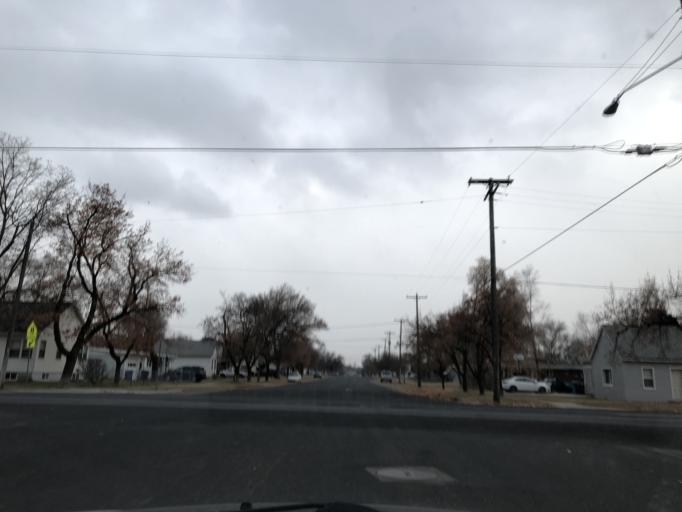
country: US
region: Utah
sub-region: Cache County
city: Logan
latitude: 41.7318
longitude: -111.8479
